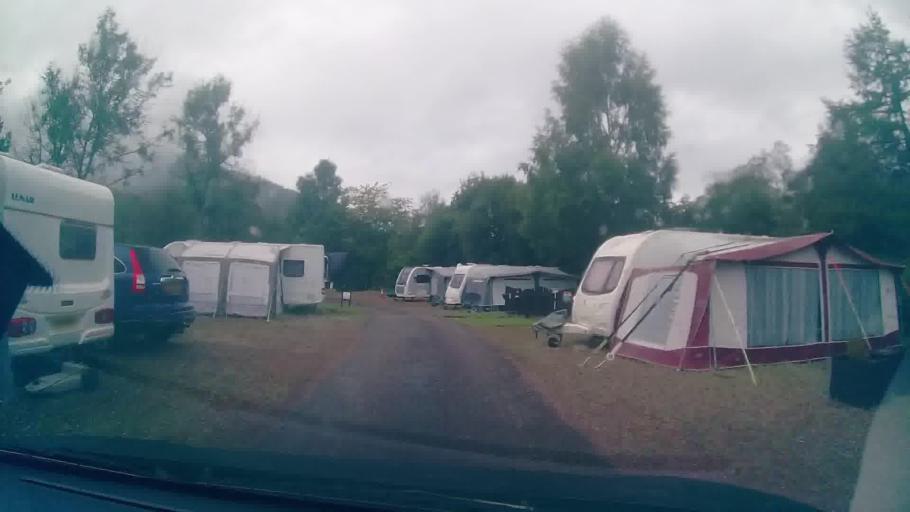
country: GB
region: Scotland
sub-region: Highland
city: Fort William
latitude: 56.6737
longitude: -5.0841
